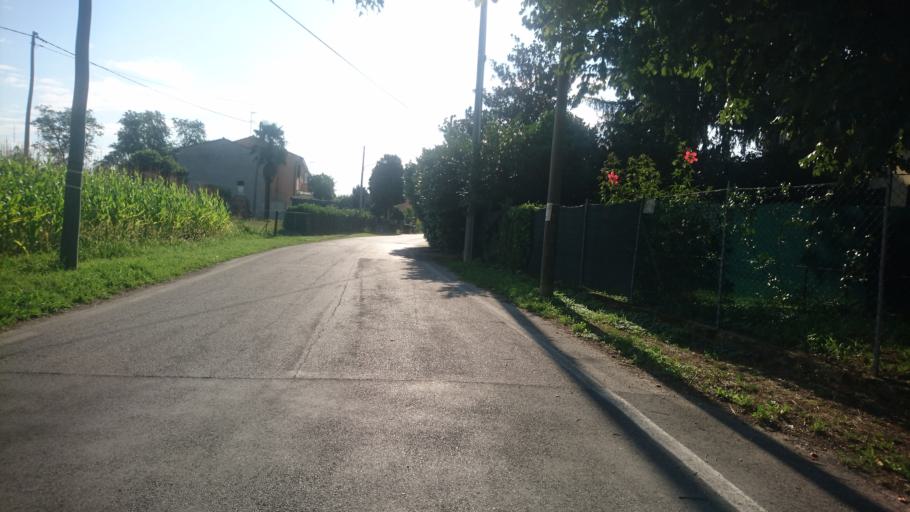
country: IT
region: Veneto
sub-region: Provincia di Padova
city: Villaguattera
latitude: 45.4347
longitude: 11.8311
